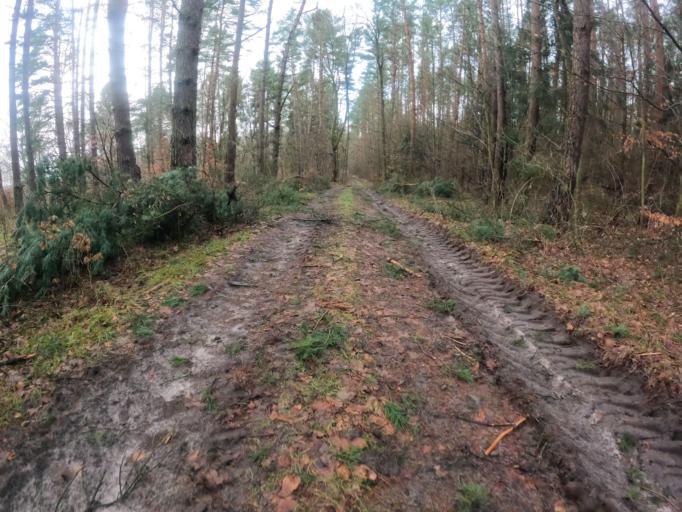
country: PL
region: West Pomeranian Voivodeship
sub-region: Powiat slawienski
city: Slawno
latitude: 54.2445
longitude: 16.6895
